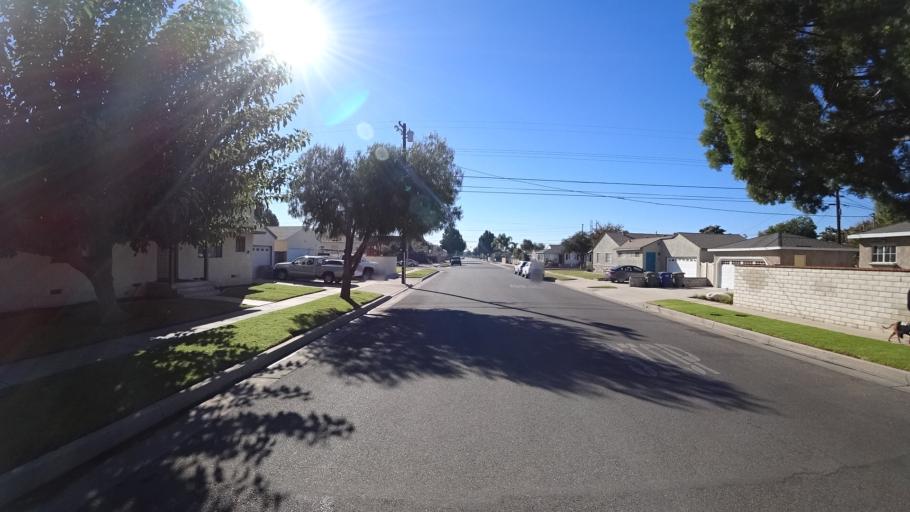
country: US
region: California
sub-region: Orange County
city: Buena Park
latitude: 33.8538
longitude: -117.9919
